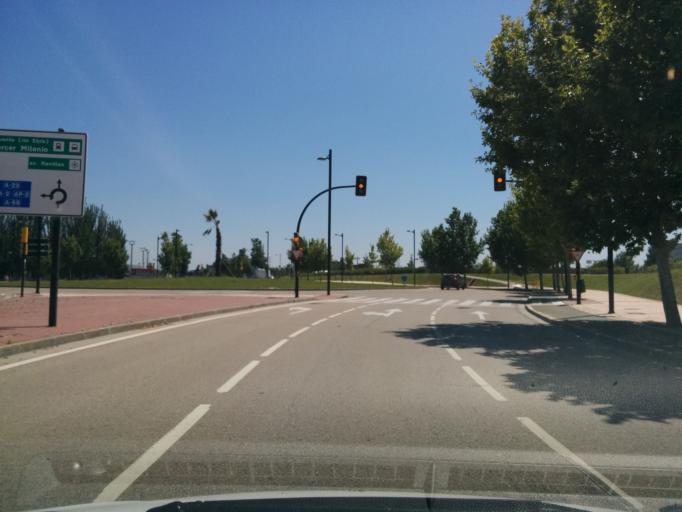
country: ES
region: Aragon
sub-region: Provincia de Zaragoza
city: Almozara
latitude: 41.6796
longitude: -0.8992
